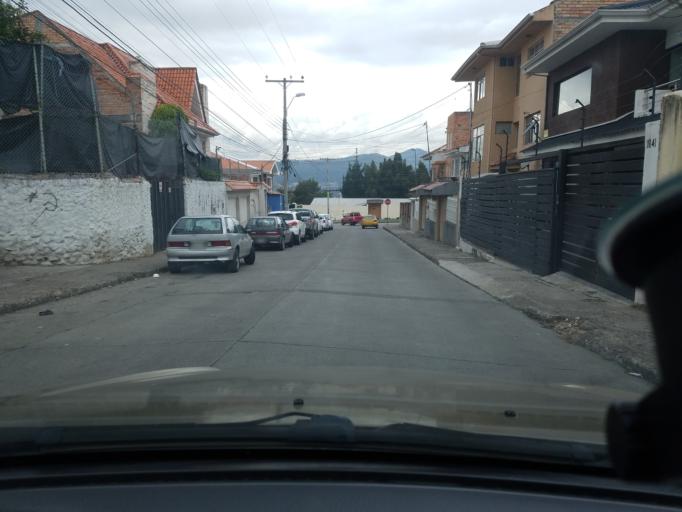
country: EC
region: Azuay
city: Cuenca
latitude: -2.8882
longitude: -79.0006
